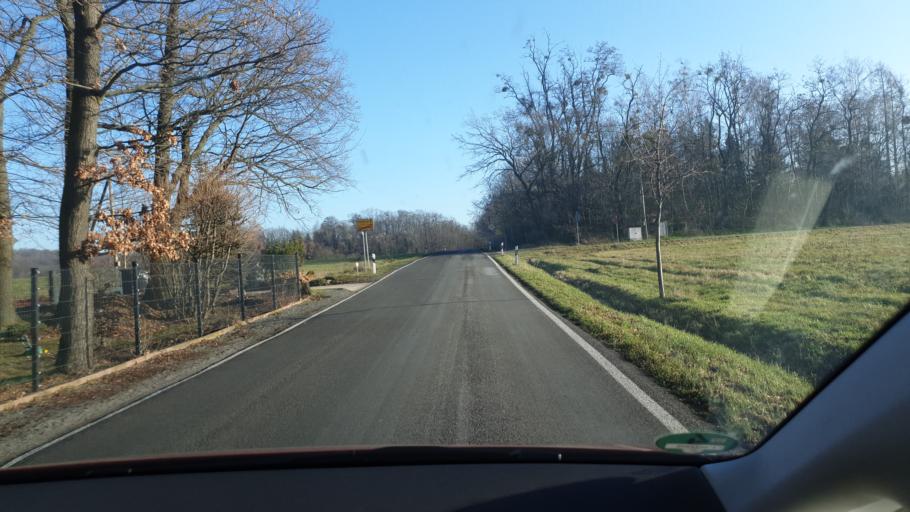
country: DE
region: Saxony
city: Hohburg
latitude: 51.4118
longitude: 12.7824
